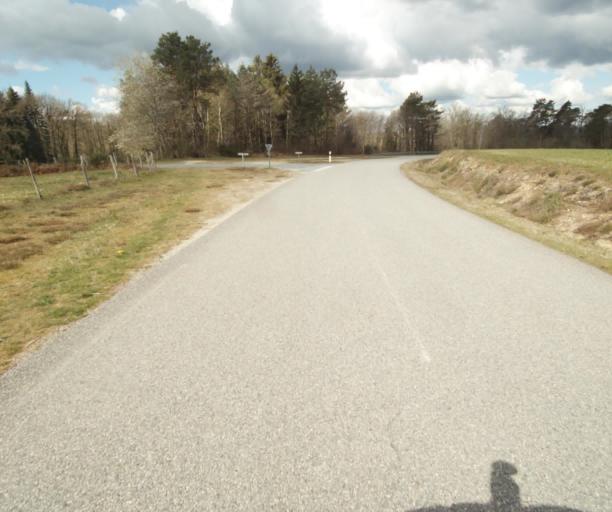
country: FR
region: Limousin
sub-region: Departement de la Correze
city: Correze
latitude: 45.3003
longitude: 1.8906
